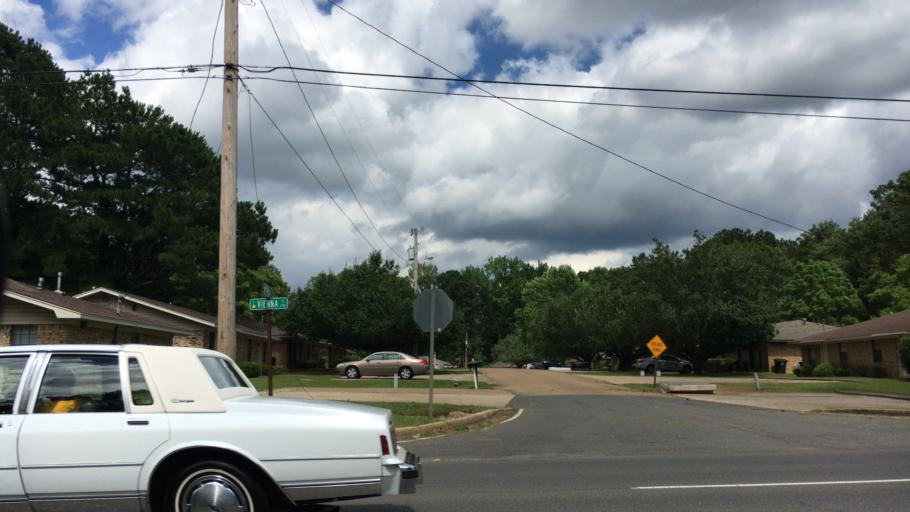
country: US
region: Louisiana
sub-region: Lincoln Parish
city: Ruston
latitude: 32.4993
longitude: -92.6368
